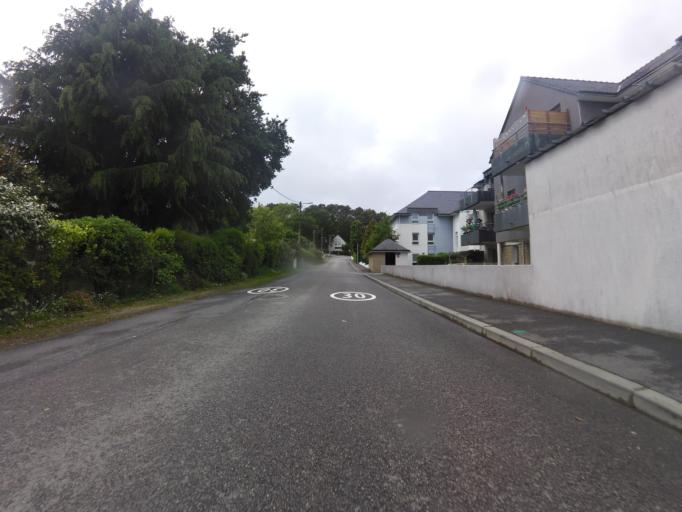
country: FR
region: Brittany
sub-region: Departement du Morbihan
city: Baden
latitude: 47.6169
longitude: -2.9213
